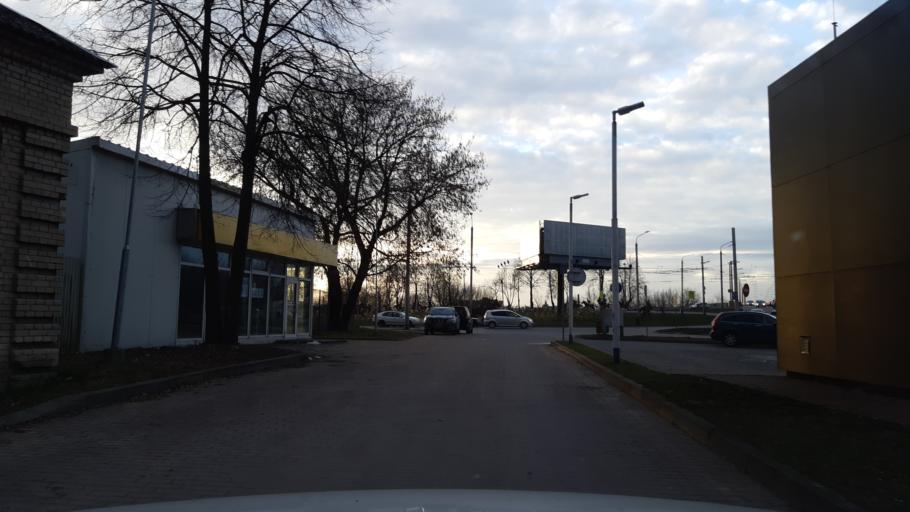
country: LT
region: Kauno apskritis
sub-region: Kaunas
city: Kaunas
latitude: 54.9014
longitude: 23.8950
